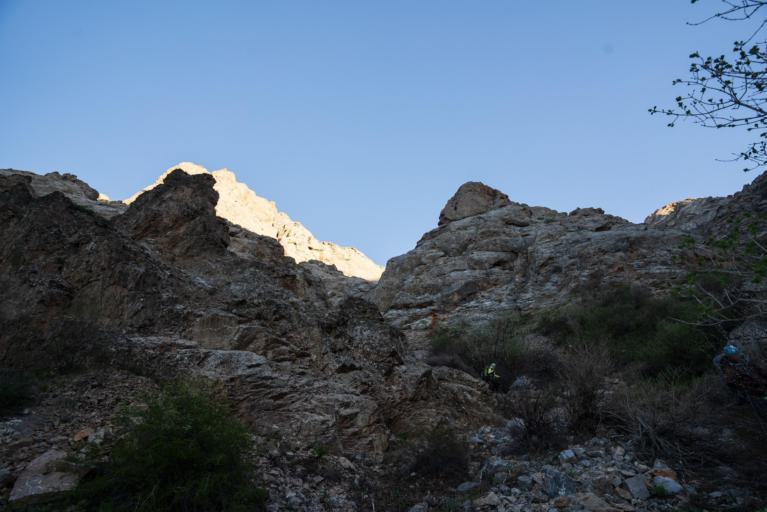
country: KZ
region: Ongtustik Qazaqstan
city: Ashchysay
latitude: 43.7661
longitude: 68.7771
